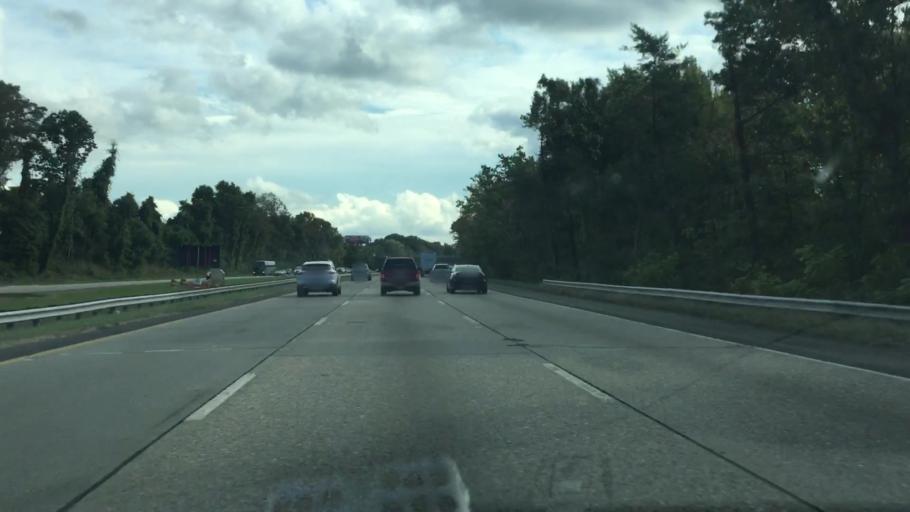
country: US
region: New Jersey
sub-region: Camden County
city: Blackwood
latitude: 39.8144
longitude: -75.0655
